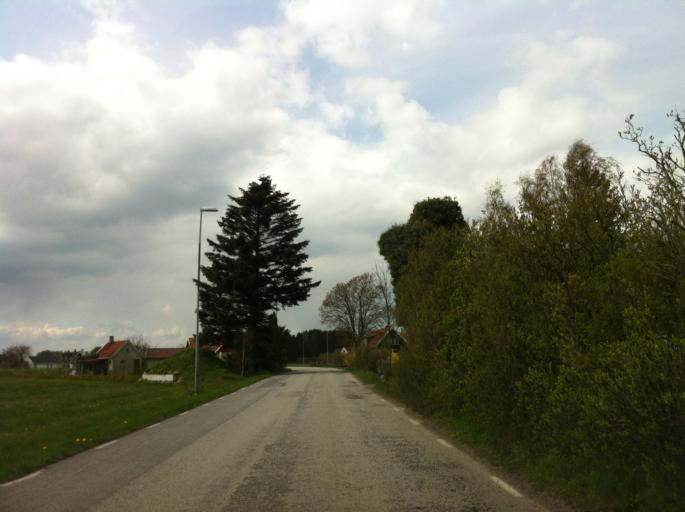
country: SE
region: Skane
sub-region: Kavlinge Kommun
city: Kaevlinge
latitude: 55.8106
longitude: 13.1443
